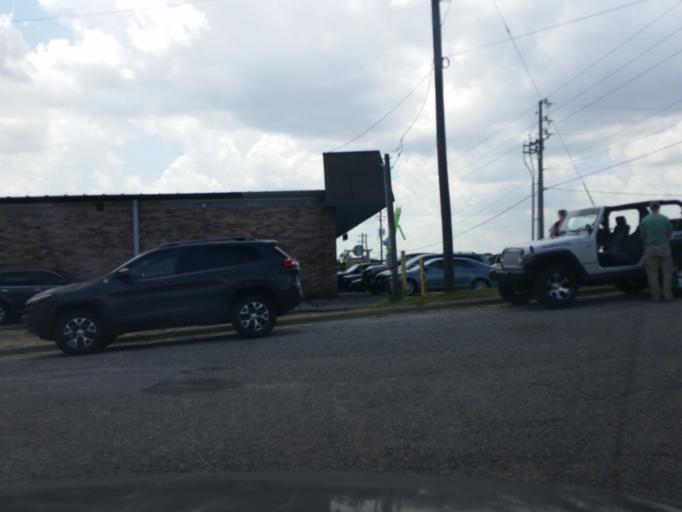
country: US
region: Florida
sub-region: Escambia County
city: Brent
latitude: 30.4740
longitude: -87.2147
